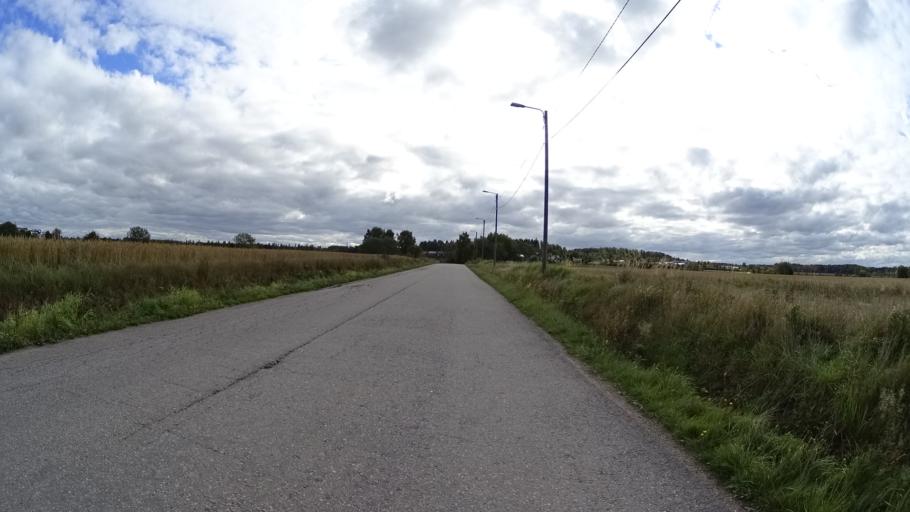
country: FI
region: Uusimaa
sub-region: Helsinki
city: Vantaa
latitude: 60.2699
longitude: 24.9564
